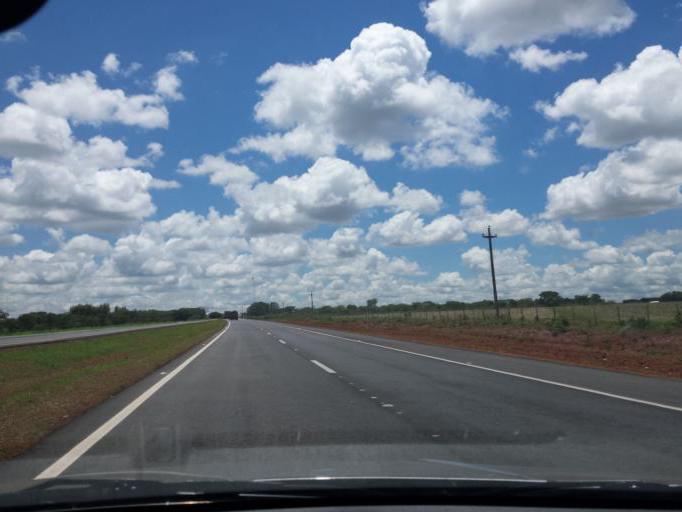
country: BR
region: Goias
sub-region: Cristalina
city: Cristalina
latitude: -16.7114
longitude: -47.6748
